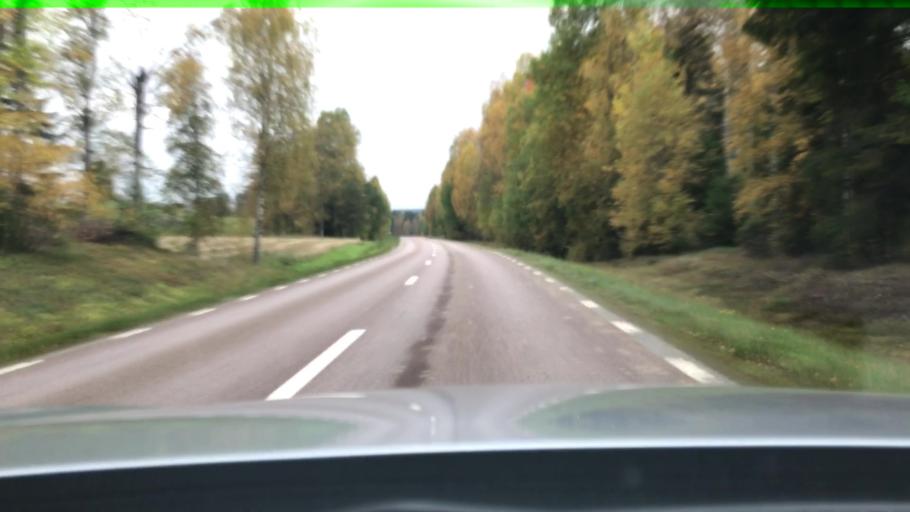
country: SE
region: Vaermland
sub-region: Eda Kommun
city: Amotfors
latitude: 59.7364
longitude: 12.2111
